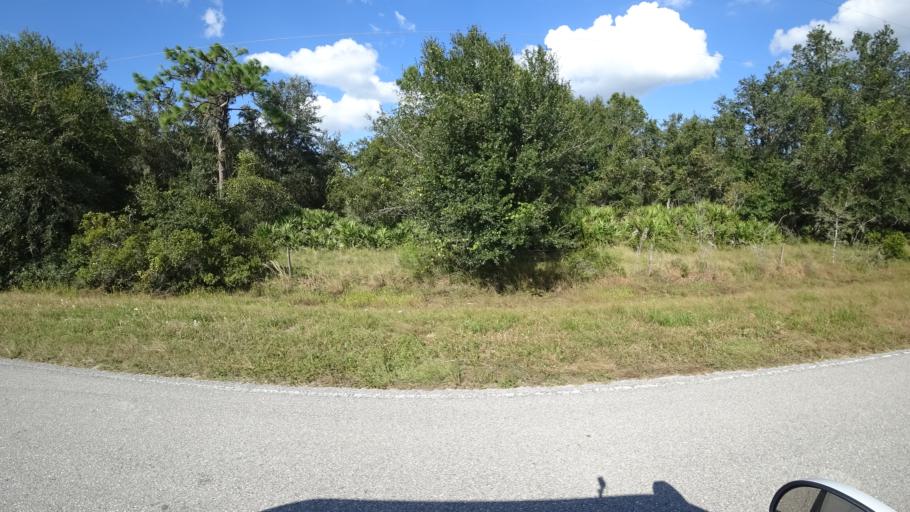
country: US
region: Florida
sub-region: DeSoto County
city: Nocatee
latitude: 27.2725
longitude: -82.1052
